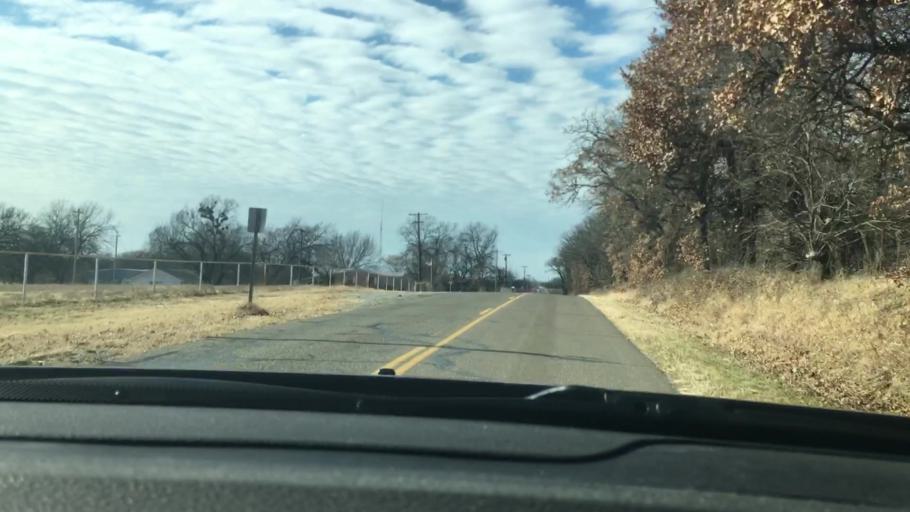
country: US
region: Oklahoma
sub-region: Garvin County
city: Pauls Valley
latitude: 34.7386
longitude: -97.1502
